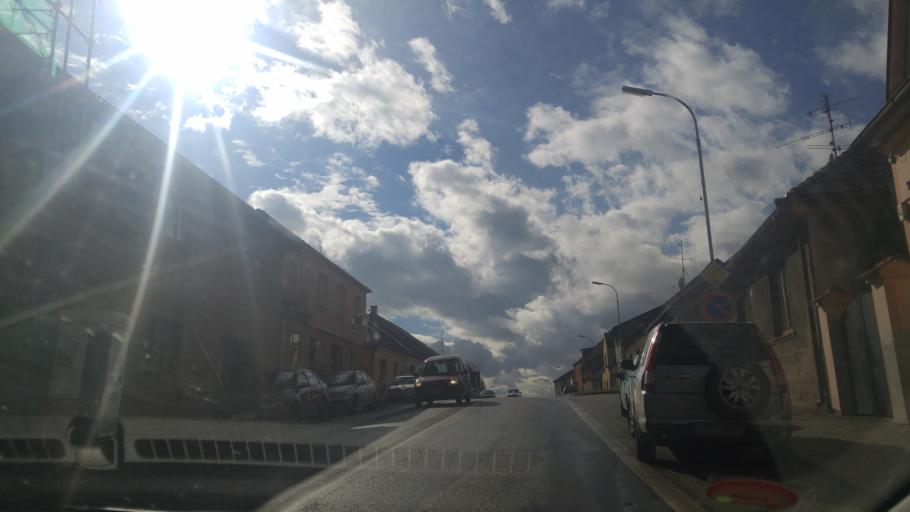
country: CZ
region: Jihocesky
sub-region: Okres Tabor
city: Veseli nad Luznici
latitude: 49.1835
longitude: 14.6970
